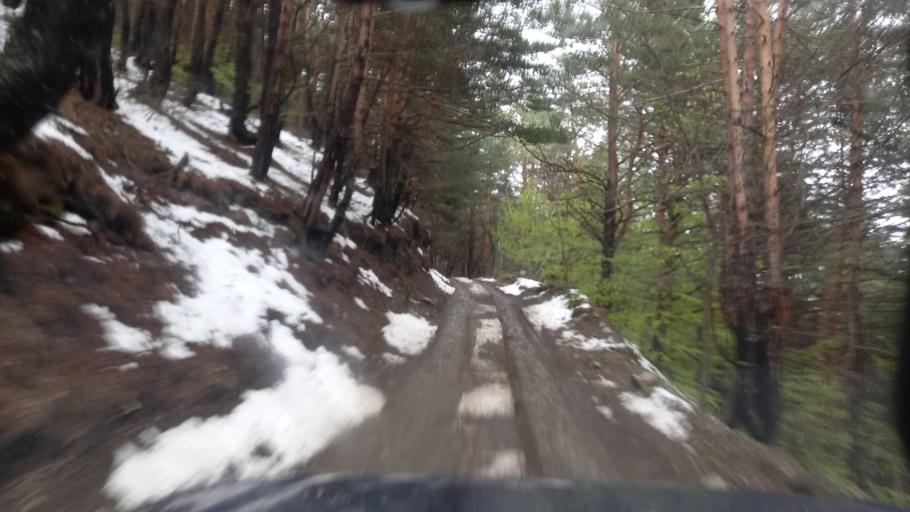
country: RU
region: North Ossetia
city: Mizur
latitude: 42.8030
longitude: 43.9609
